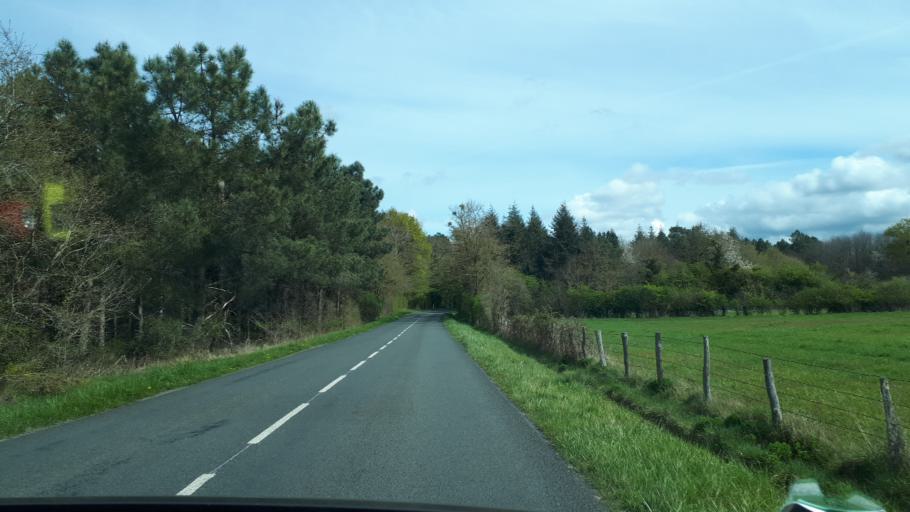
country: FR
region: Pays de la Loire
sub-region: Departement de la Sarthe
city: Ecommoy
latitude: 47.8541
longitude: 0.2902
